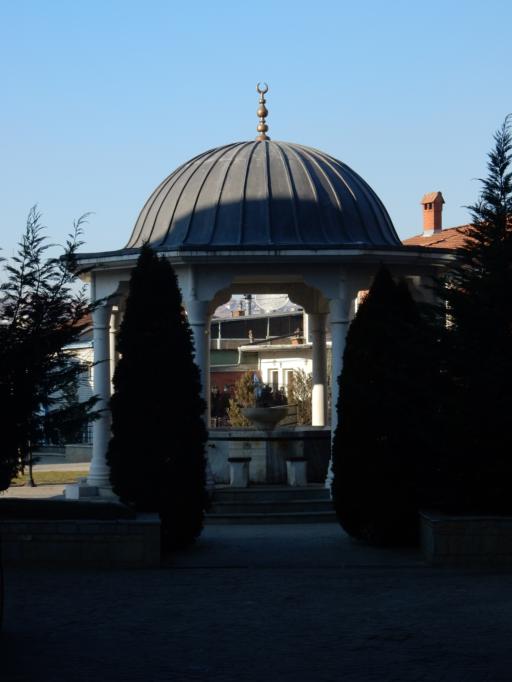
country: XK
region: Pristina
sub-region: Komuna e Prishtines
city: Pristina
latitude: 42.6669
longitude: 21.1670
